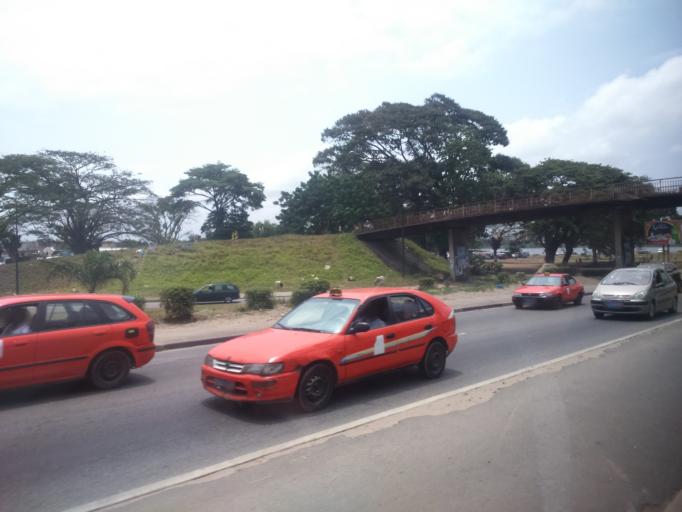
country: CI
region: Lagunes
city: Abidjan
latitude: 5.3109
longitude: -4.0054
